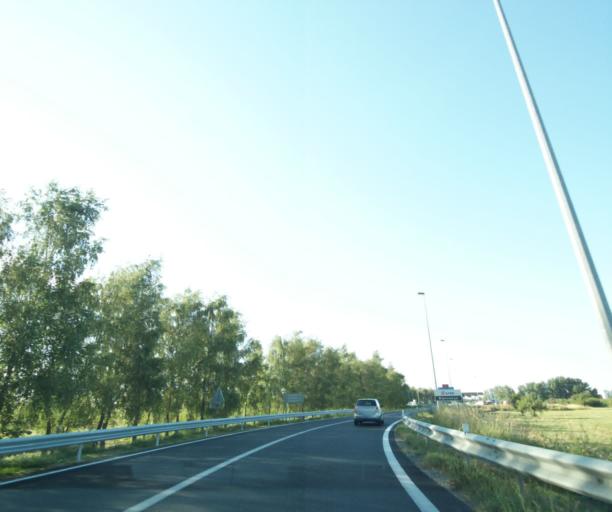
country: FR
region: Ile-de-France
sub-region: Departement de Seine-et-Marne
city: Marolles-sur-Seine
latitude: 48.3824
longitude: 3.0192
